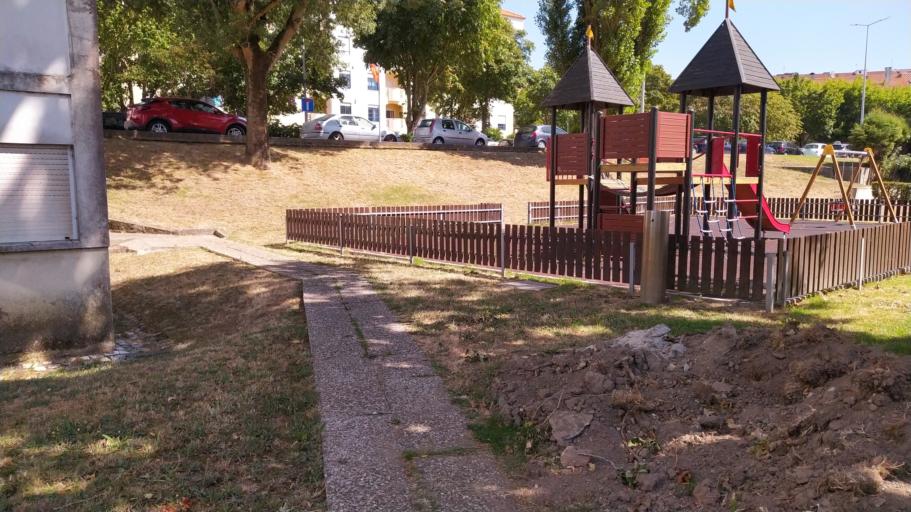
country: PT
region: Aveiro
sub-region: Aveiro
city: Aveiro
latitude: 40.6477
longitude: -8.6411
